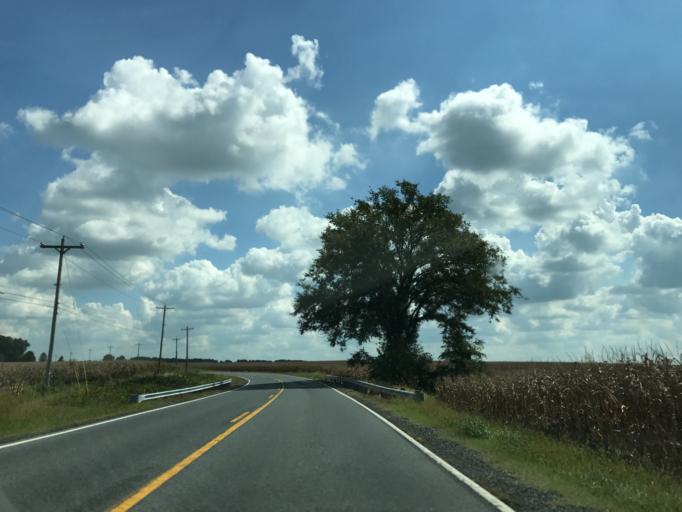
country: US
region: Maryland
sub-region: Queen Anne's County
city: Centreville
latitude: 39.0043
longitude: -75.9747
